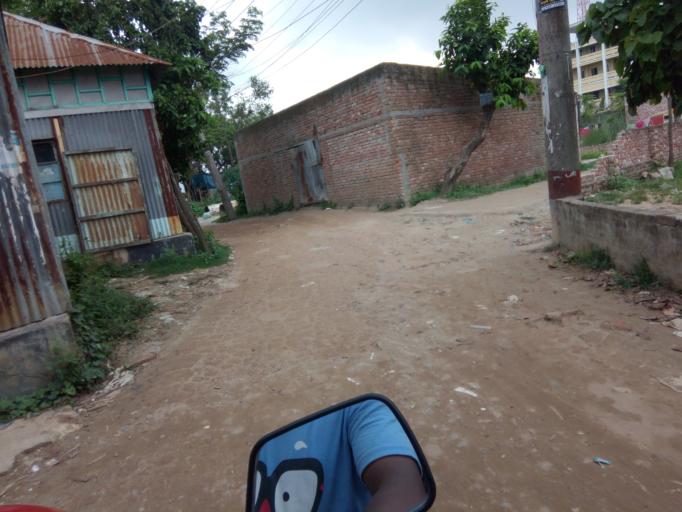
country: BD
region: Dhaka
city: Paltan
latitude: 23.7399
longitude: 90.4617
